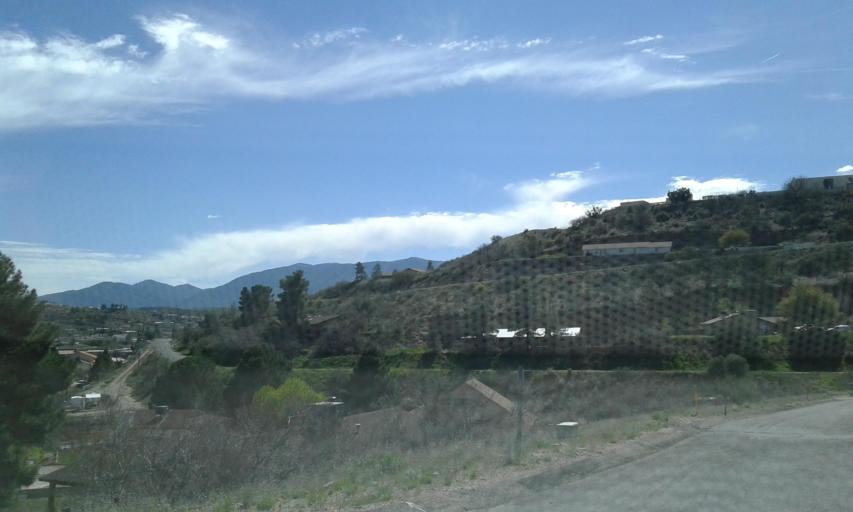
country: US
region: Arizona
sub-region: Gila County
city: Central Heights-Midland City
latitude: 33.4257
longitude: -110.8131
